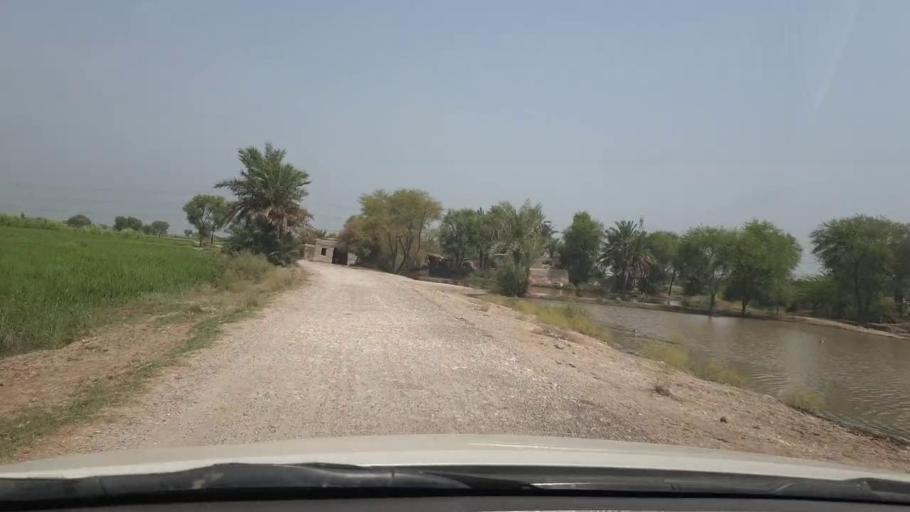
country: PK
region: Sindh
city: Shikarpur
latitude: 28.0235
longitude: 68.6465
